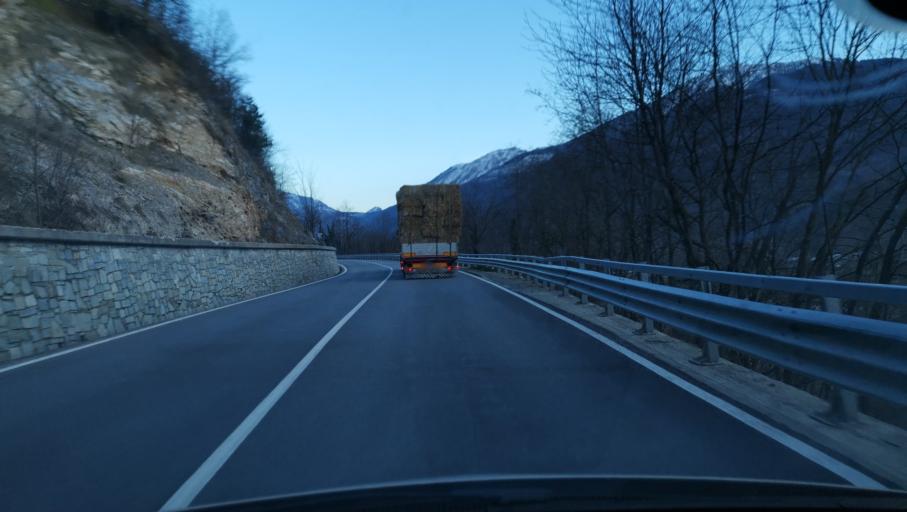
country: IT
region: Piedmont
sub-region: Provincia di Cuneo
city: Demonte
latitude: 44.3144
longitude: 7.2748
